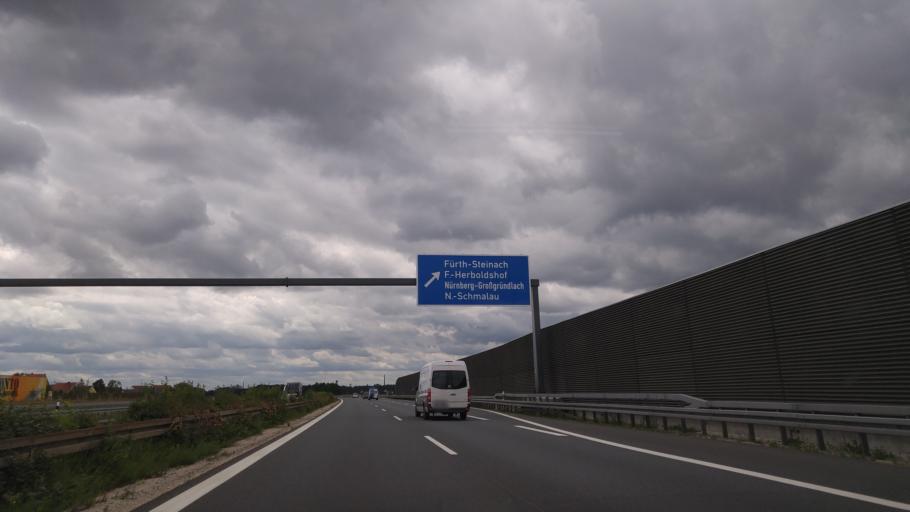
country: DE
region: Bavaria
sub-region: Regierungsbezirk Mittelfranken
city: Furth
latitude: 49.5198
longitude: 10.9919
